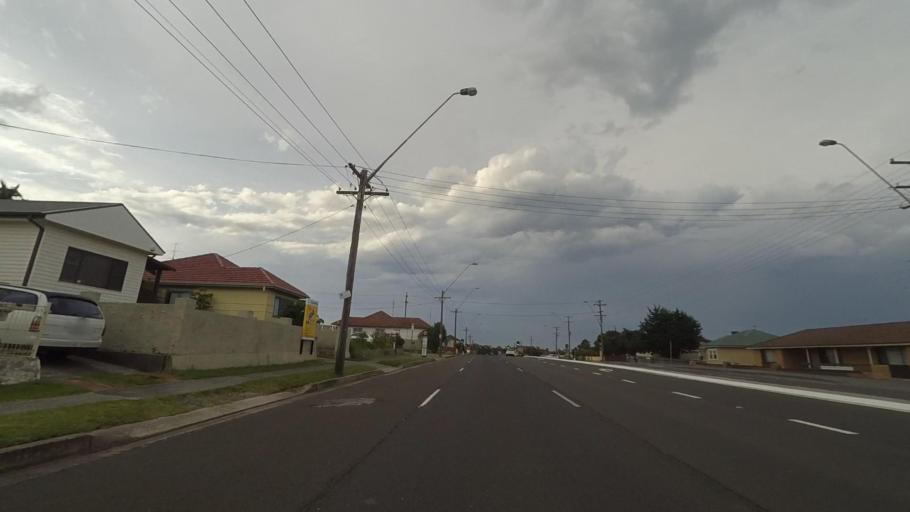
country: AU
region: New South Wales
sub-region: Shellharbour
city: Lake Illawarra
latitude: -34.5560
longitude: 150.8596
